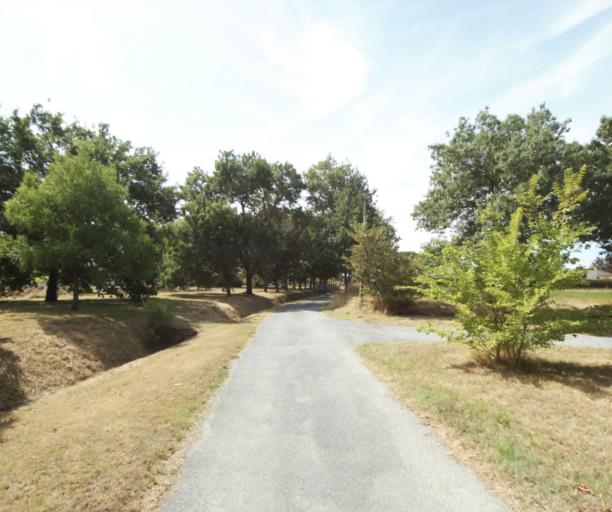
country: FR
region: Midi-Pyrenees
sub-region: Departement de la Haute-Garonne
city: Revel
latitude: 43.5105
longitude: 2.0361
